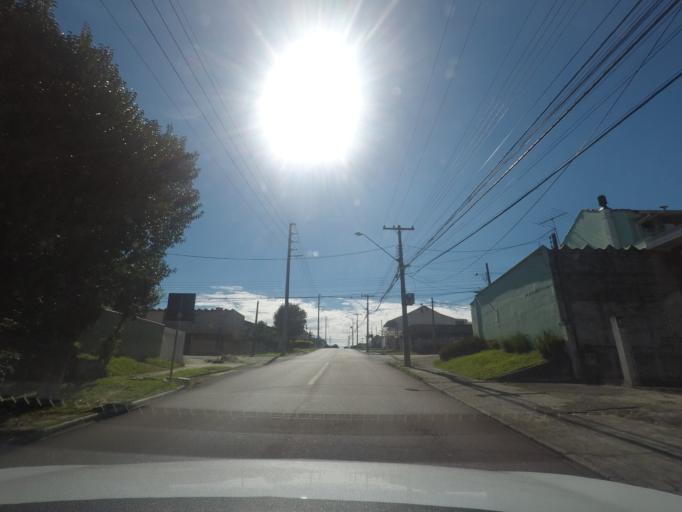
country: BR
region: Parana
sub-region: Sao Jose Dos Pinhais
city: Sao Jose dos Pinhais
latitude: -25.5039
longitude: -49.2770
